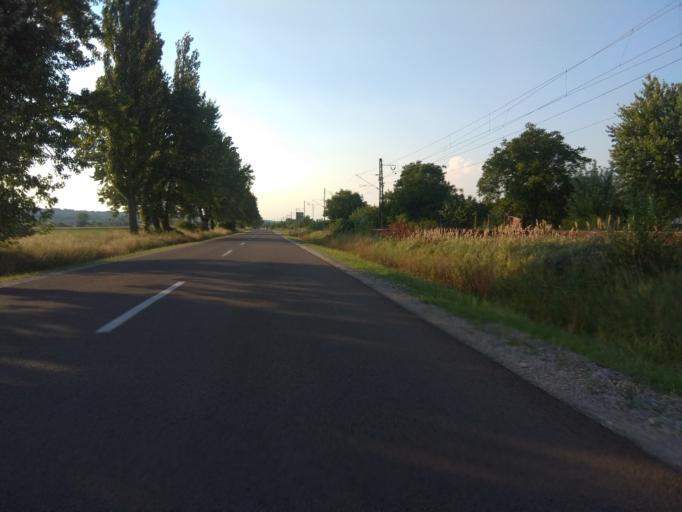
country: HU
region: Borsod-Abauj-Zemplen
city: Nyekladhaza
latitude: 47.9793
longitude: 20.8456
